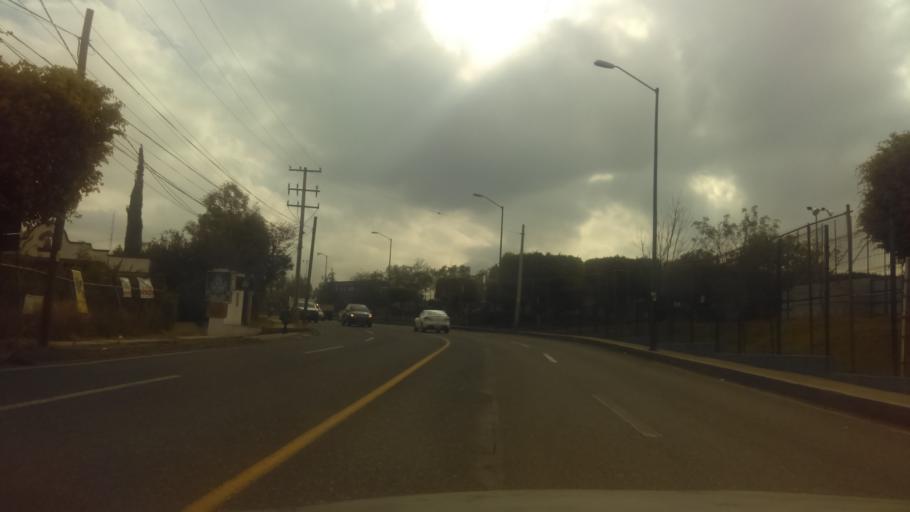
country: MX
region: Michoacan
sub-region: Morelia
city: Montana Monarca (Punta Altozano)
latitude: 19.6756
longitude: -101.1845
